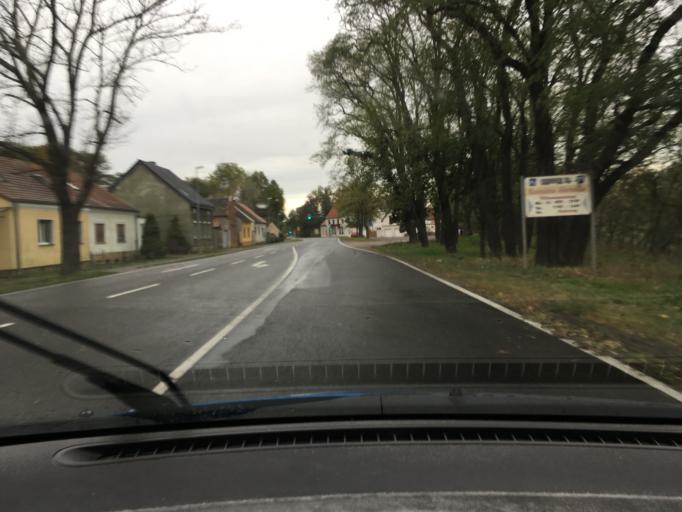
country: DE
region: Saxony-Anhalt
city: Zerbst
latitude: 51.9345
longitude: 12.1318
